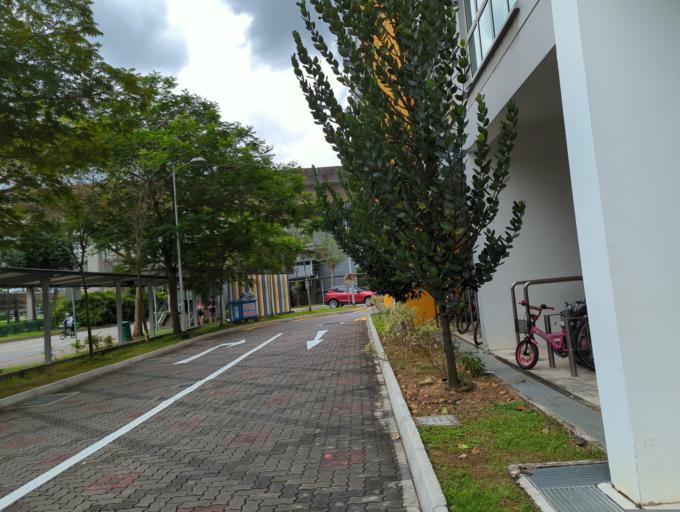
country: MY
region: Johor
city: Kampung Pasir Gudang Baru
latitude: 1.3905
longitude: 103.8945
